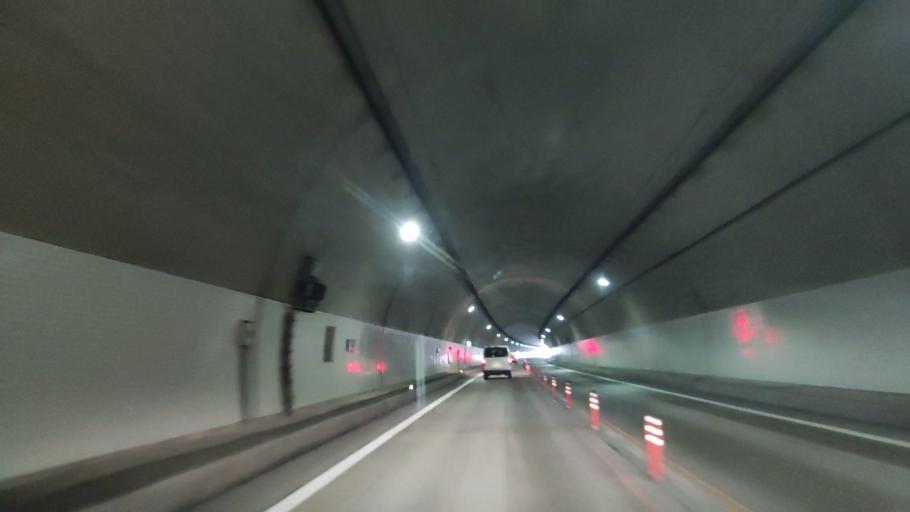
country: JP
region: Akita
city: Odate
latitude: 40.3315
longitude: 140.6096
